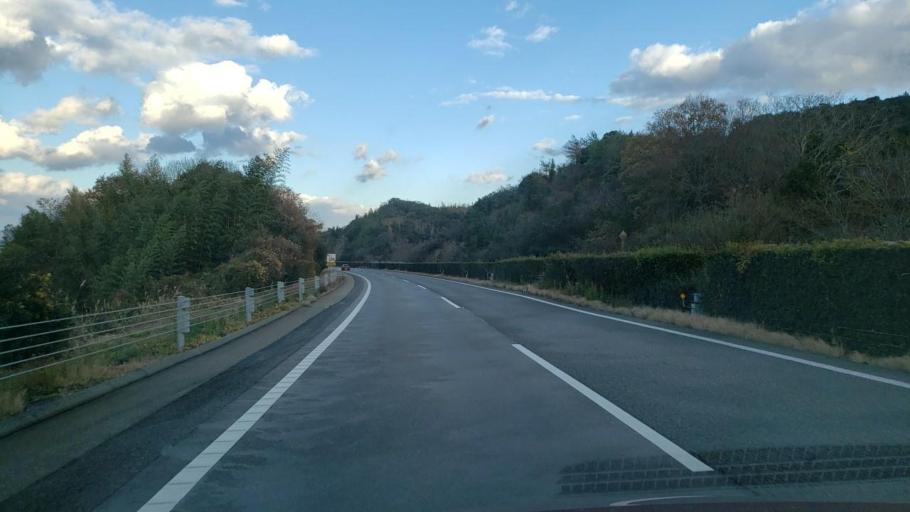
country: JP
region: Hyogo
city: Fukura
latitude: 34.2889
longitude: 134.7214
